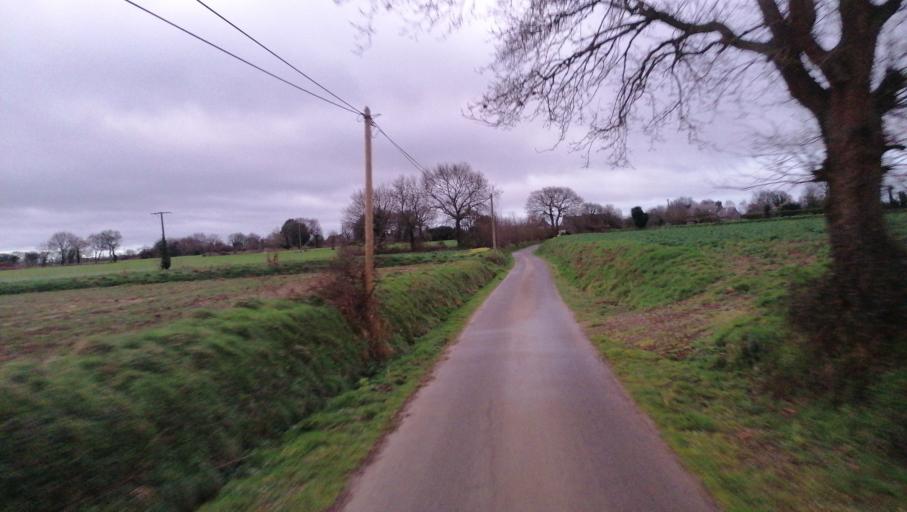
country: FR
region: Brittany
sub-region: Departement des Cotes-d'Armor
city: Plehedel
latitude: 48.6686
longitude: -3.0298
